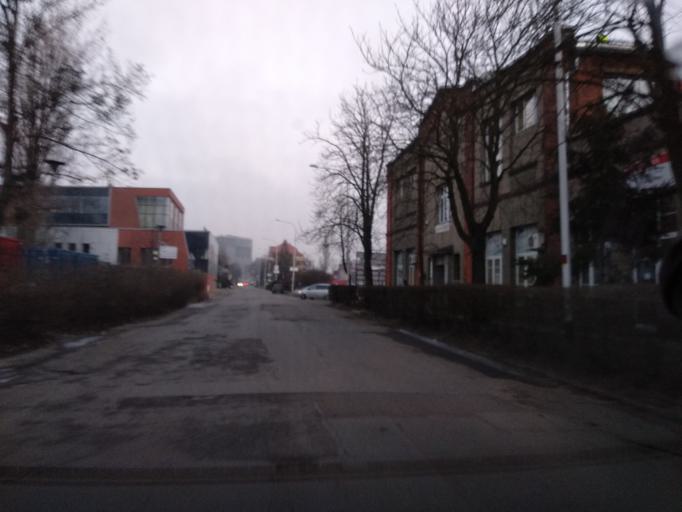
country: PL
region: Lower Silesian Voivodeship
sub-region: Powiat wroclawski
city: Wroclaw
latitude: 51.1123
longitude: 16.9849
